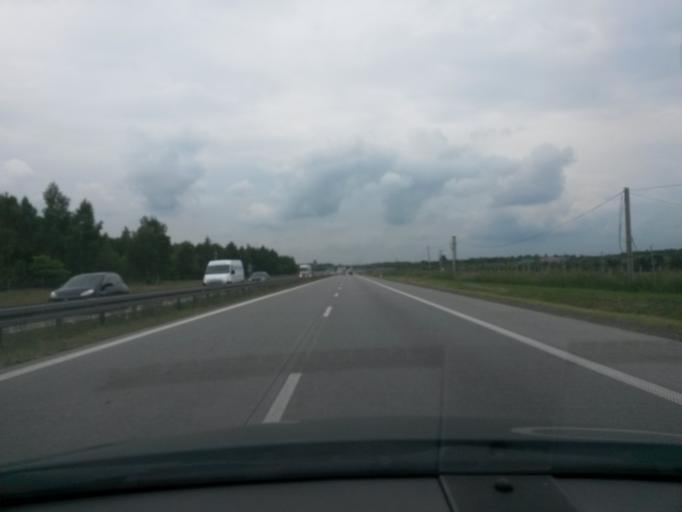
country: PL
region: Lodz Voivodeship
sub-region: Powiat skierniewicki
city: Kowiesy
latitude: 51.8723
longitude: 20.3865
